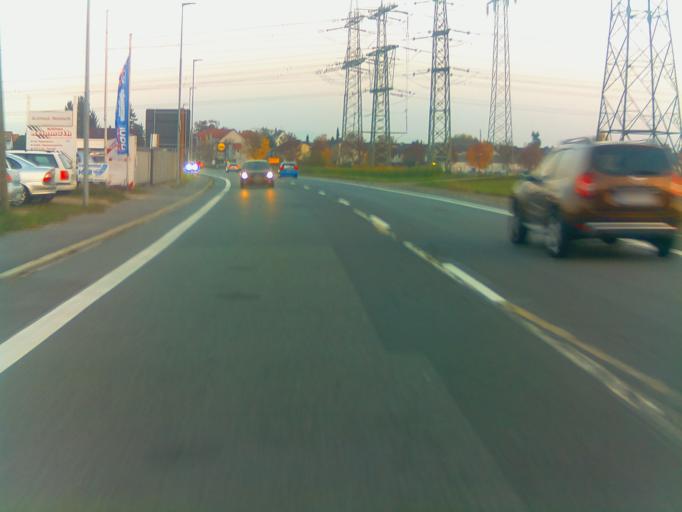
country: DE
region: Baden-Wuerttemberg
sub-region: Karlsruhe Region
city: Ilvesheim
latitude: 49.4822
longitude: 8.5471
